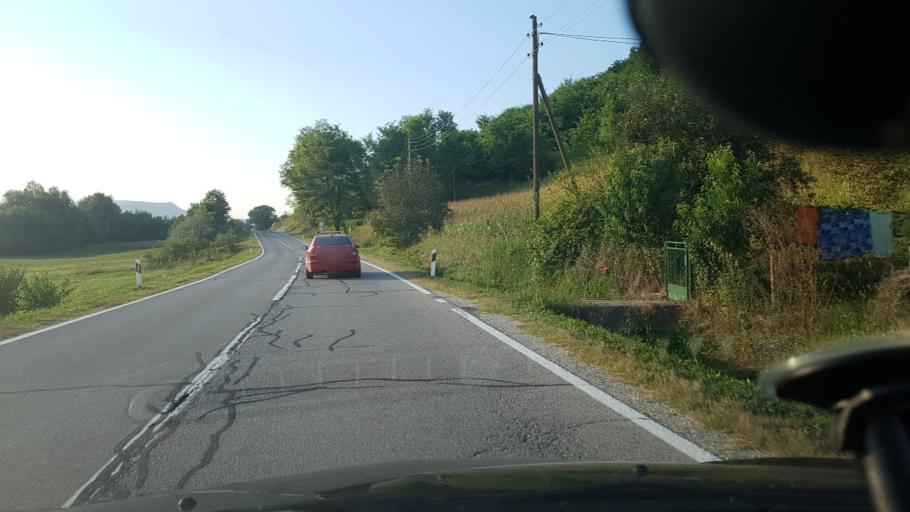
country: HR
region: Krapinsko-Zagorska
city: Pregrada
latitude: 46.1310
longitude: 15.7989
